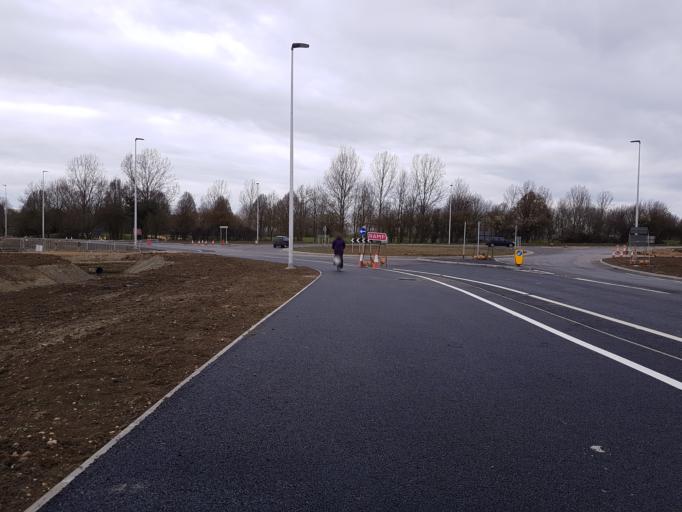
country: GB
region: England
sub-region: Cambridgeshire
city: Girton
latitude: 52.2454
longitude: 0.0401
